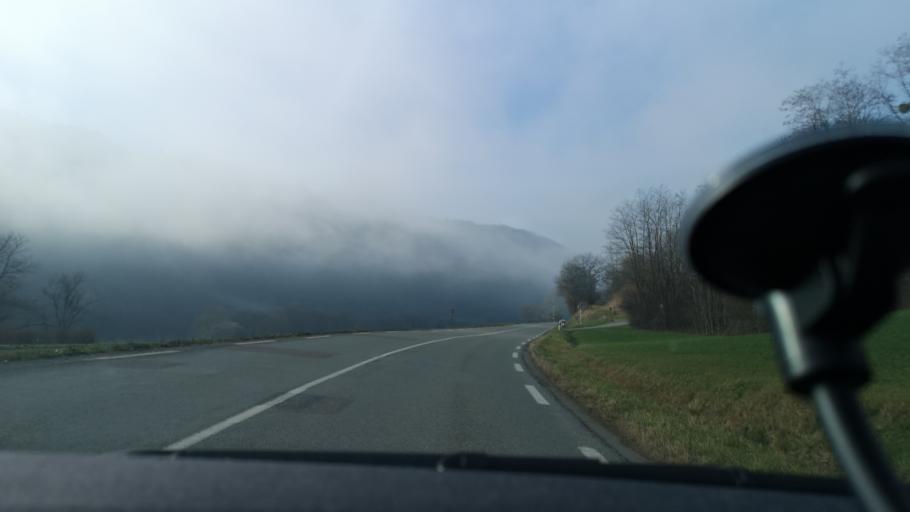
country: FR
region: Franche-Comte
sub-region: Departement du Doubs
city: Baume-les-Dames
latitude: 47.3599
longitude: 6.4160
